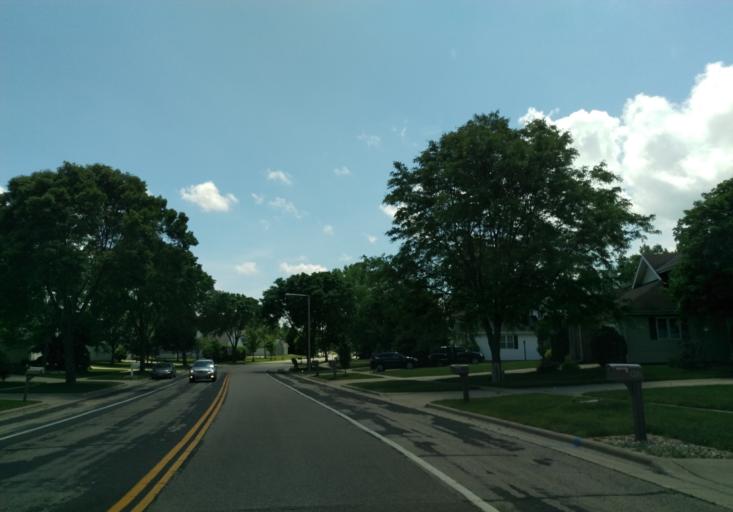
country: US
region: Wisconsin
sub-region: Dane County
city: Middleton
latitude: 43.0848
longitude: -89.5203
